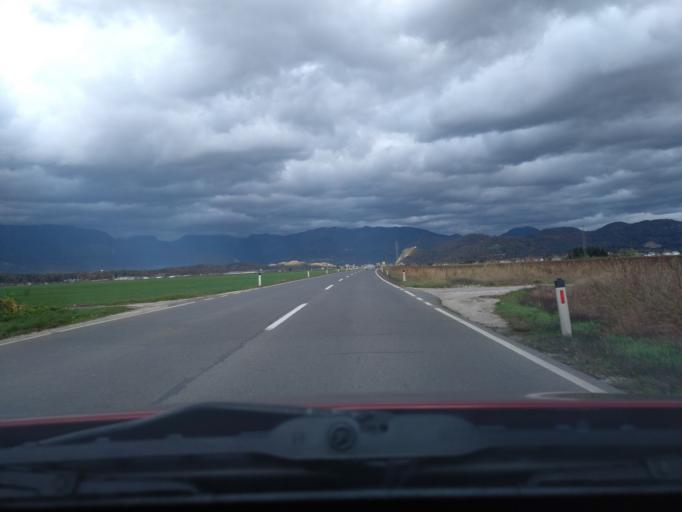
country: SI
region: Menges
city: Menges
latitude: 46.1807
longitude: 14.5814
